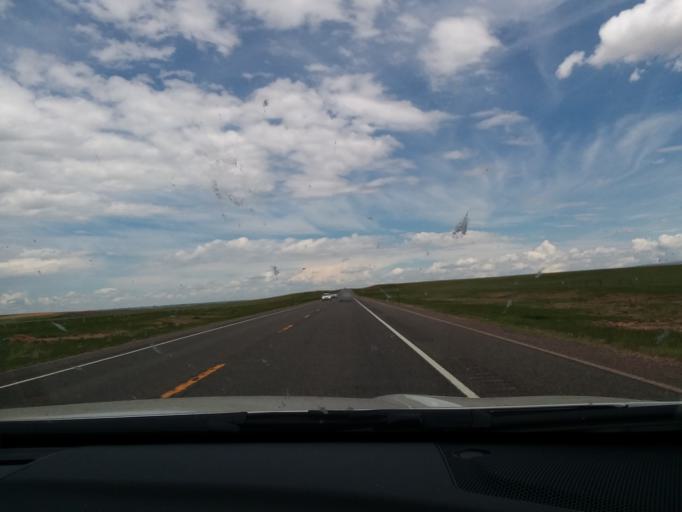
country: US
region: Wyoming
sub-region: Albany County
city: Laramie
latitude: 41.2047
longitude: -105.5990
